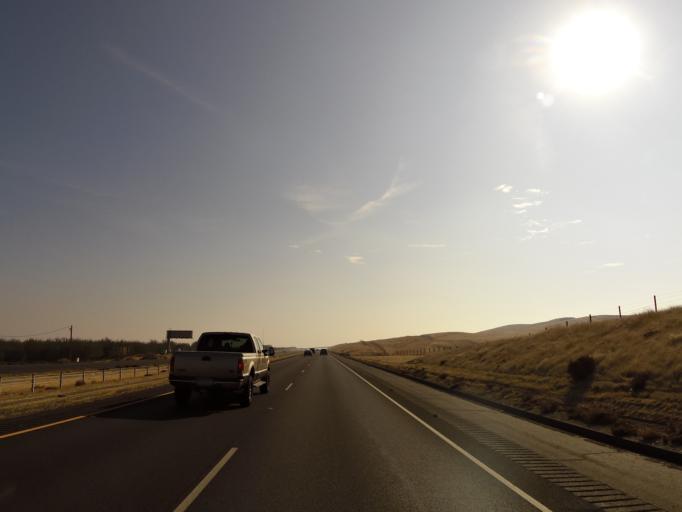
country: US
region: California
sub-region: Kings County
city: Avenal
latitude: 36.0614
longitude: -120.0768
